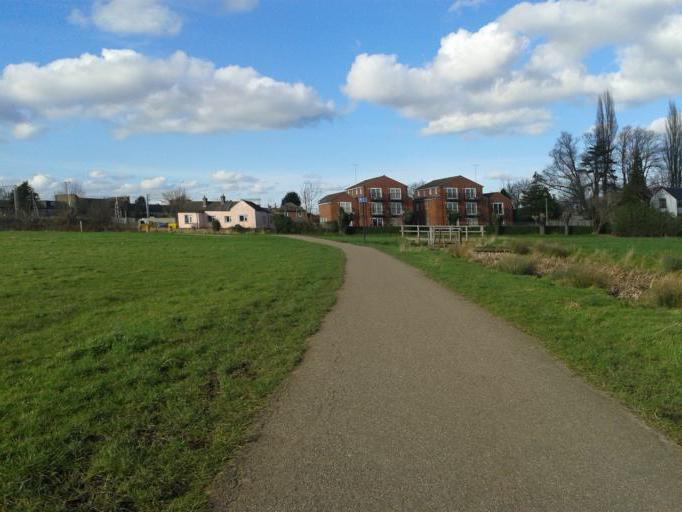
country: GB
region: England
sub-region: Cambridgeshire
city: Cambridge
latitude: 52.2194
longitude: 0.1586
